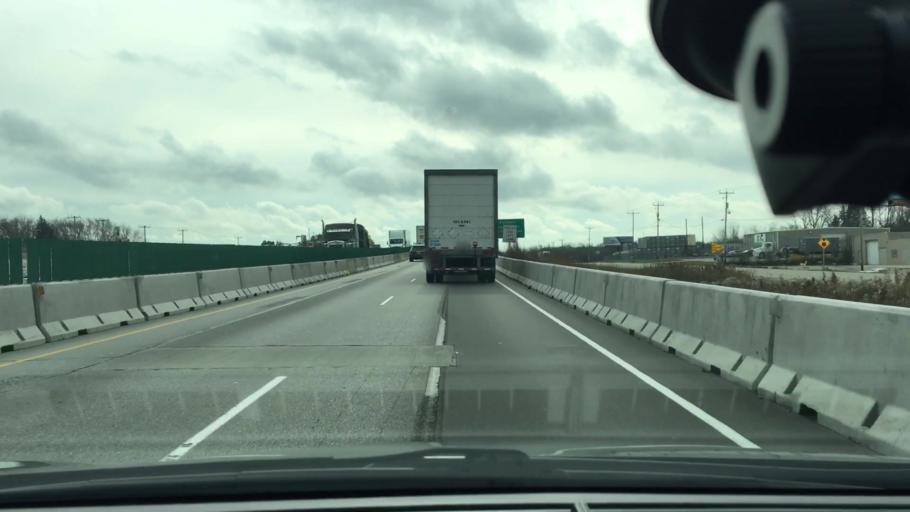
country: US
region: Wisconsin
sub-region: Racine County
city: Franksville
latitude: 42.7455
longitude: -87.9543
